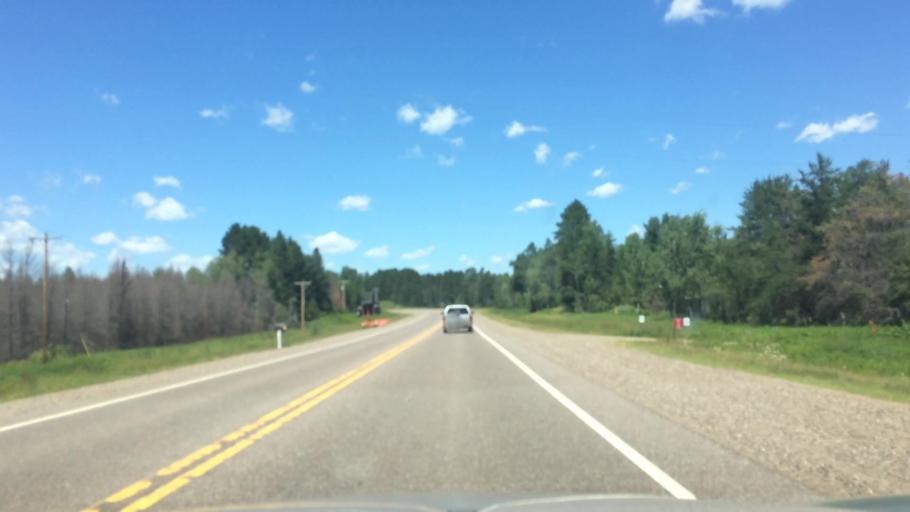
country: US
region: Wisconsin
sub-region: Lincoln County
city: Tomahawk
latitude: 45.6525
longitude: -89.7049
